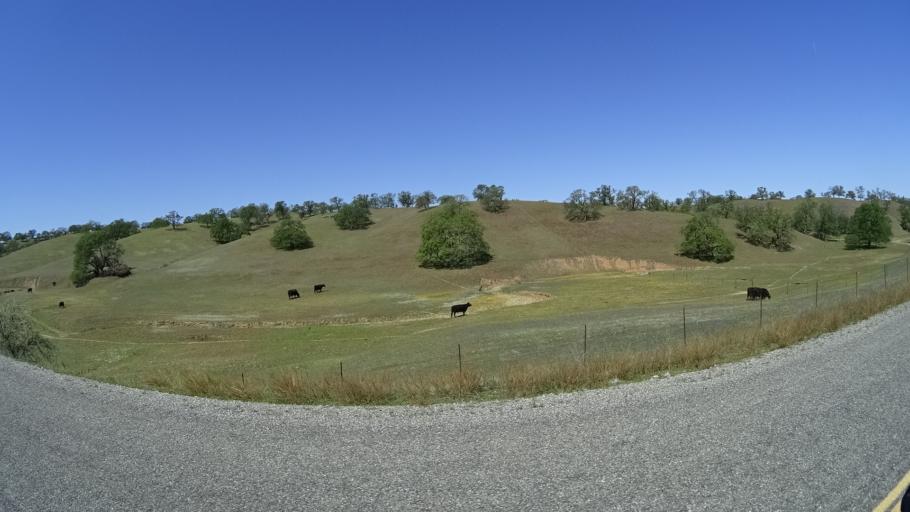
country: US
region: California
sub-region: Glenn County
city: Orland
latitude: 39.7463
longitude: -122.3689
